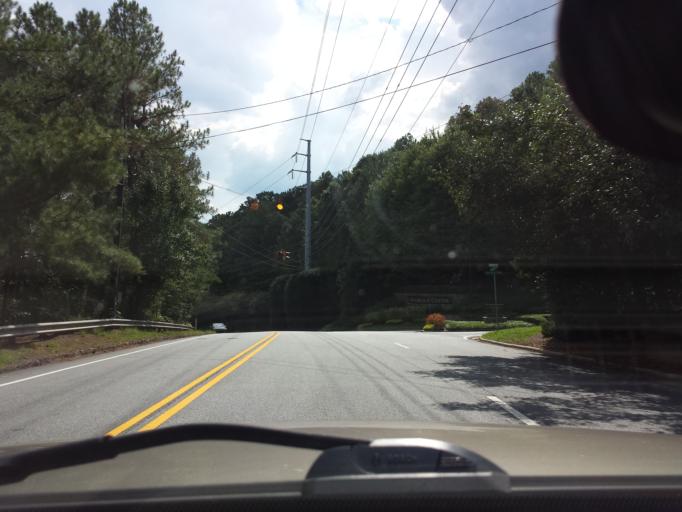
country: US
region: Georgia
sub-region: Fulton County
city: Sandy Springs
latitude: 33.9106
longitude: -84.4322
